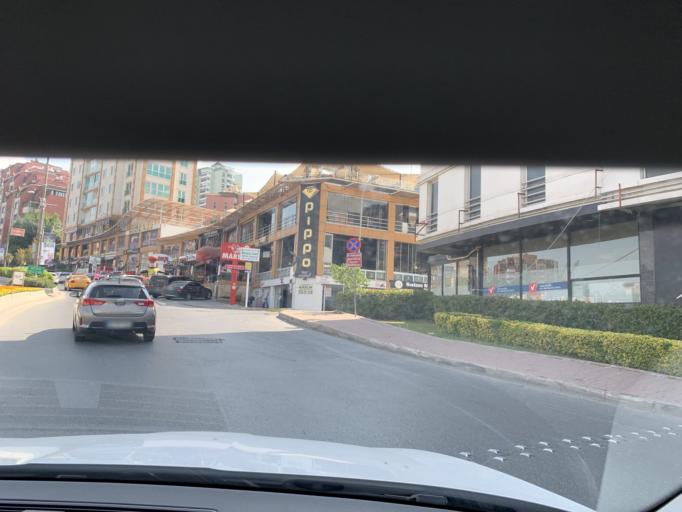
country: TR
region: Istanbul
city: Esenyurt
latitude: 41.0697
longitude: 28.6841
